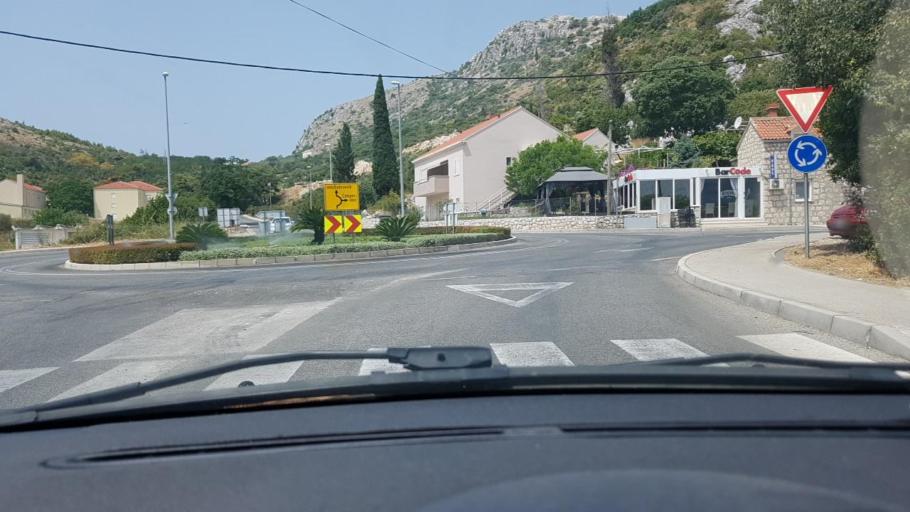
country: HR
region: Dubrovacko-Neretvanska
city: Cibaca
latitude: 42.6305
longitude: 18.1618
